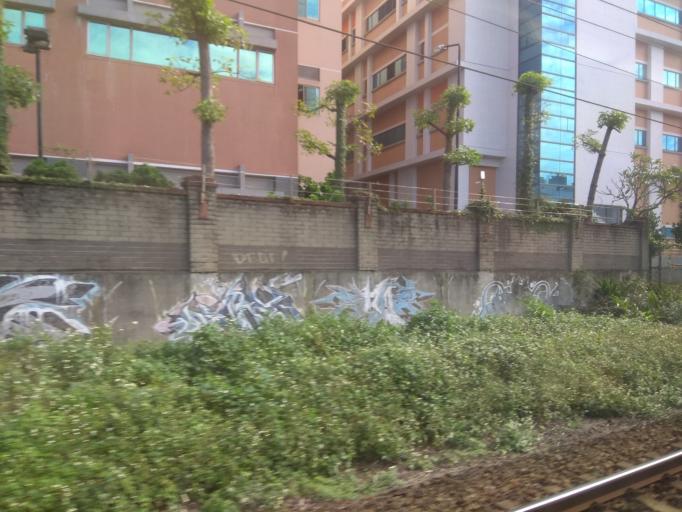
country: TW
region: Taiwan
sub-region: Taoyuan
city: Taoyuan
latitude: 24.9847
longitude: 121.3258
